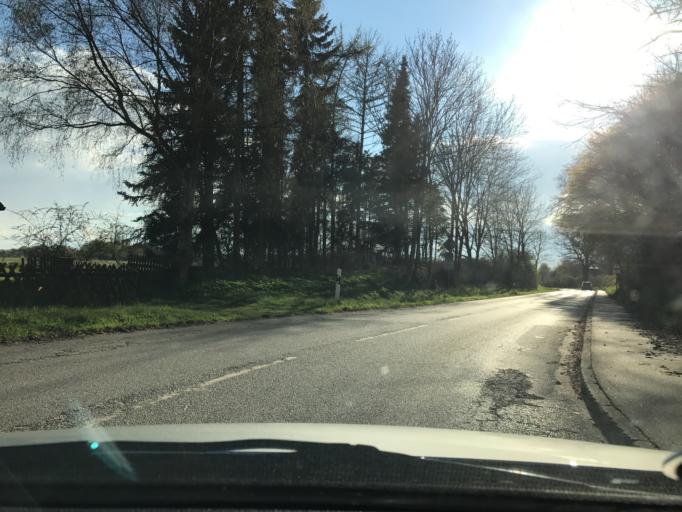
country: DE
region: Schleswig-Holstein
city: Kuhren
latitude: 54.1697
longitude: 10.2652
